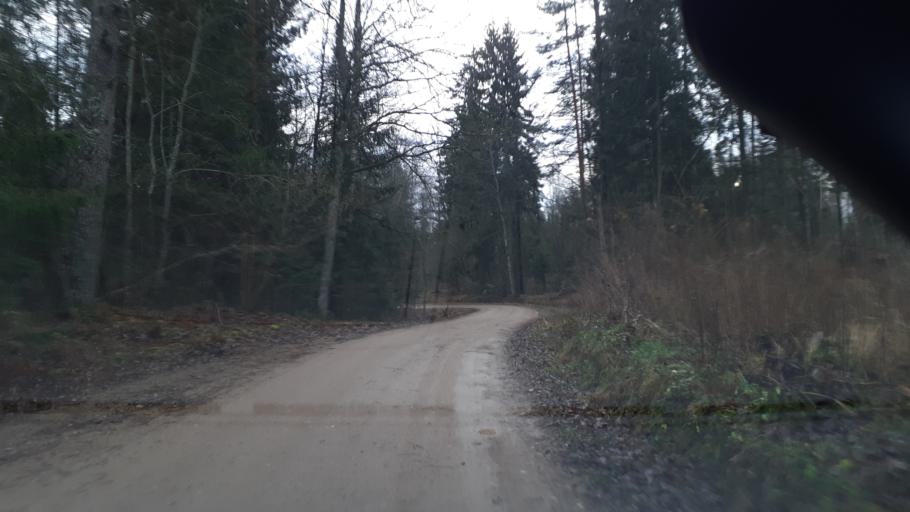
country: LV
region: Kuldigas Rajons
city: Kuldiga
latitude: 56.9015
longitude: 21.9095
